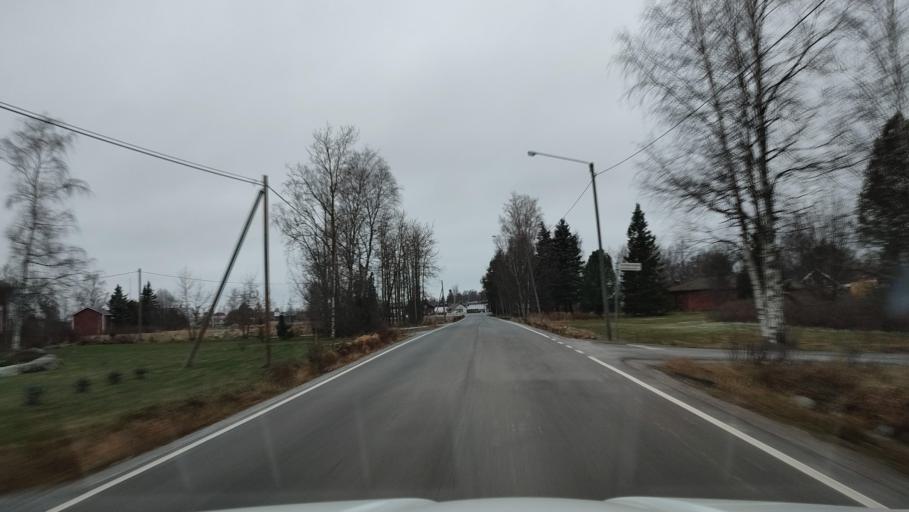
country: FI
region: Ostrobothnia
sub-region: Sydosterbotten
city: Kristinestad
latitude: 62.2497
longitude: 21.5263
